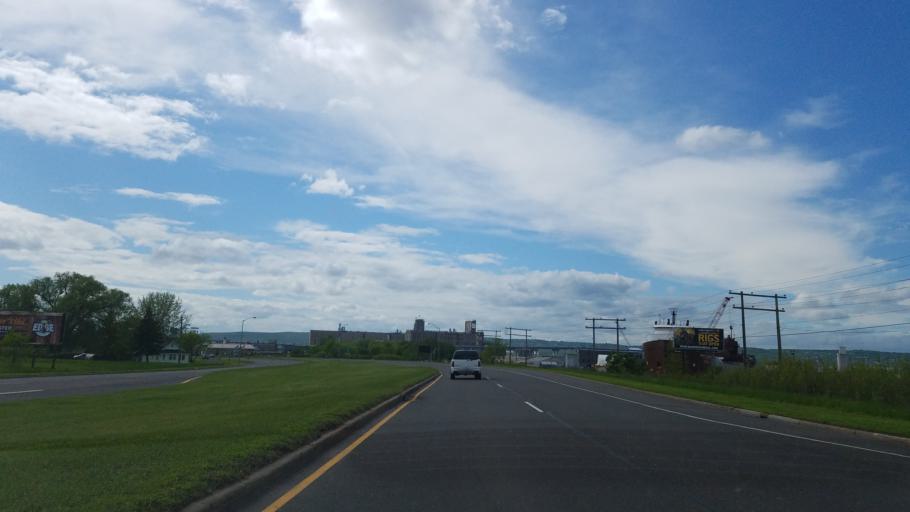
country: US
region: Wisconsin
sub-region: Douglas County
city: Superior
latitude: 46.7323
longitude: -92.0847
